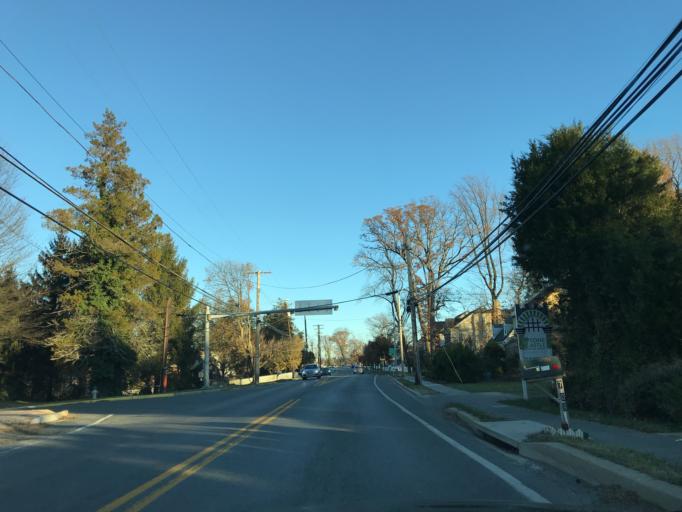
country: US
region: Maryland
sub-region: Montgomery County
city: Ashton-Sandy Spring
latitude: 39.1495
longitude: -77.0259
